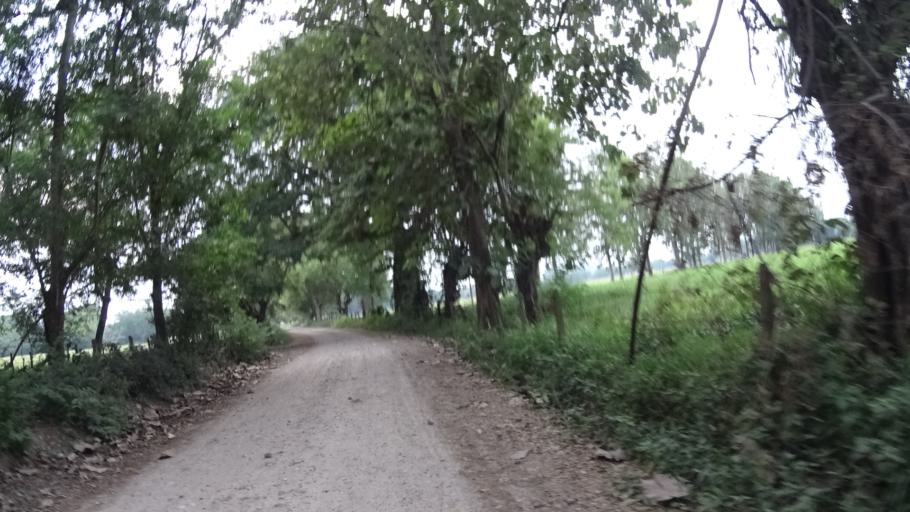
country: CO
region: Cundinamarca
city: Puerto Salgar
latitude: 5.4810
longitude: -74.6846
